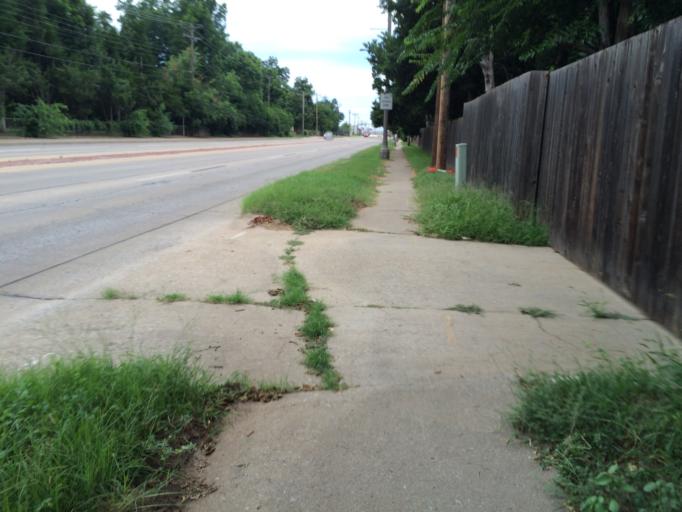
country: US
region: Oklahoma
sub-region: Cleveland County
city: Norman
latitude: 35.2186
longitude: -97.4648
